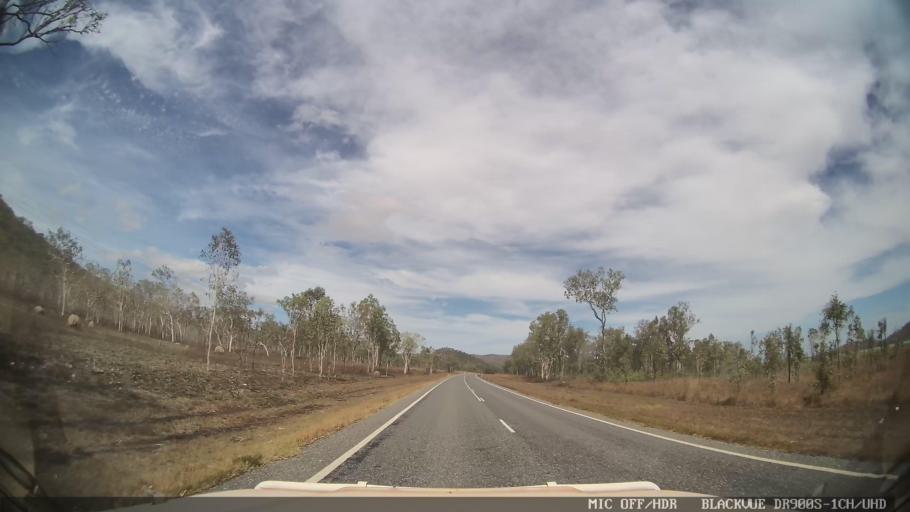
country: AU
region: Queensland
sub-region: Tablelands
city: Mareeba
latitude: -16.7852
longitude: 145.3495
